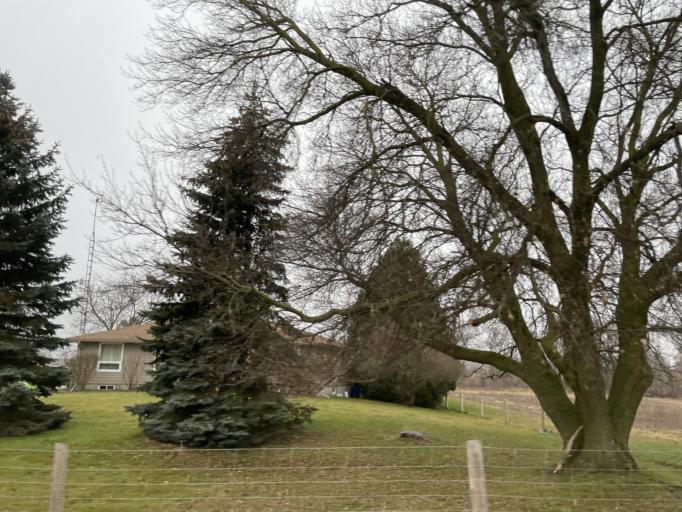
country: CA
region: Ontario
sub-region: Wellington County
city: Guelph
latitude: 43.4879
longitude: -80.3406
